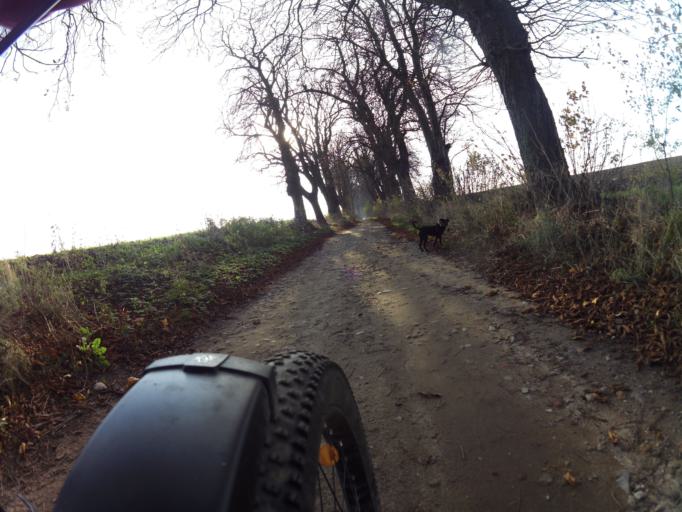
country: PL
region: Pomeranian Voivodeship
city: Strzelno
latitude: 54.7567
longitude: 18.2917
